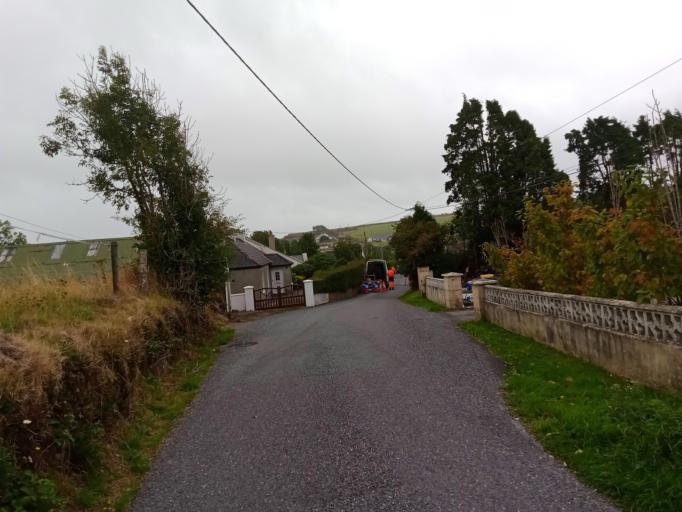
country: IE
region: Munster
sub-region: Waterford
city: Dungarvan
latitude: 52.0482
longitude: -7.5694
